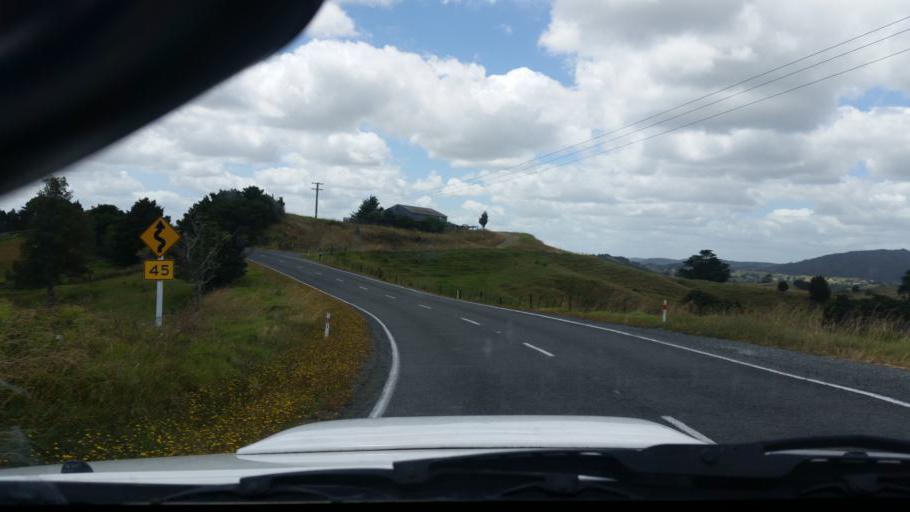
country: NZ
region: Northland
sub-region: Whangarei
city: Ruakaka
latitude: -36.0598
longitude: 174.2727
